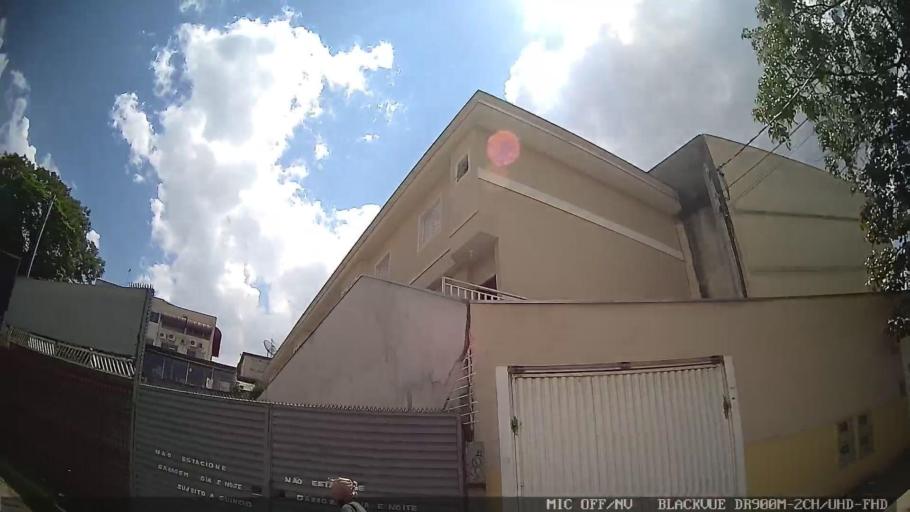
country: BR
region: Sao Paulo
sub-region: Ferraz De Vasconcelos
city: Ferraz de Vasconcelos
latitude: -23.5403
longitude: -46.4512
